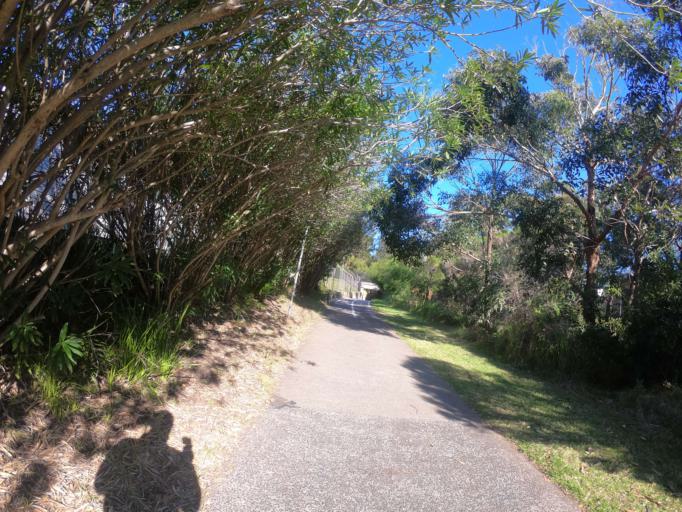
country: AU
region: New South Wales
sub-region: Wollongong
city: Corrimal
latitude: -34.3900
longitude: 150.9072
